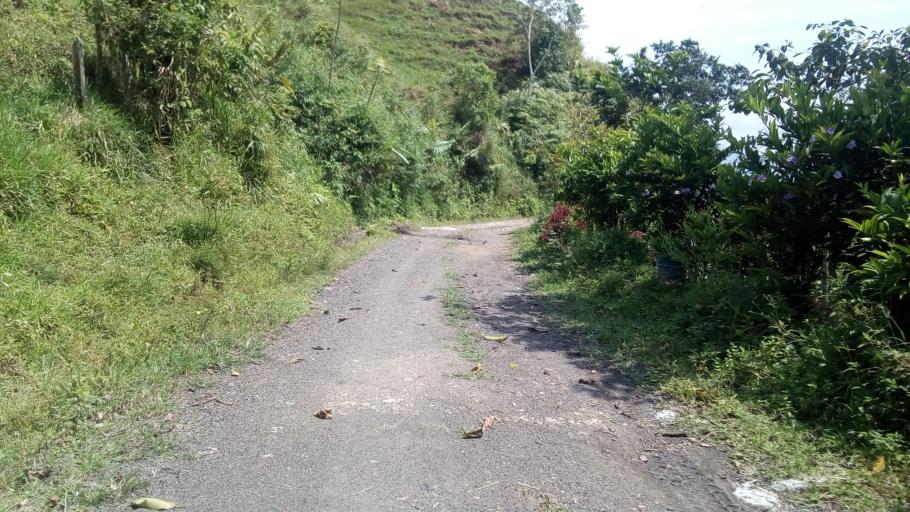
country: CO
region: Boyaca
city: Otanche
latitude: 5.6240
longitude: -74.2342
